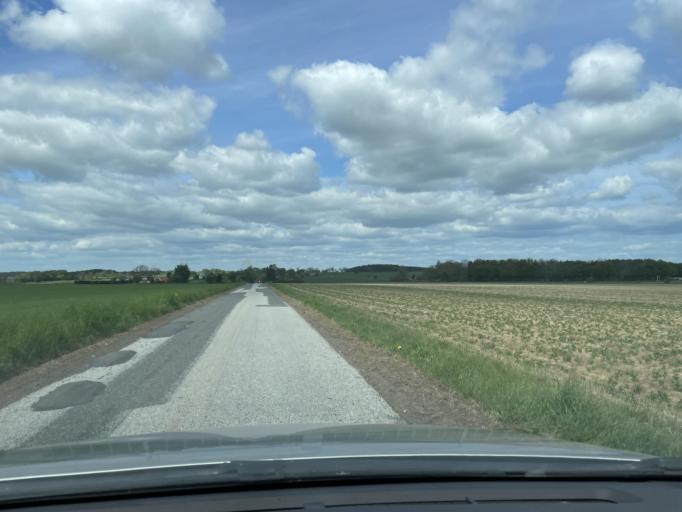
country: DK
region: Central Jutland
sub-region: Odder Kommune
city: Odder
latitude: 55.9058
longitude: 10.1198
